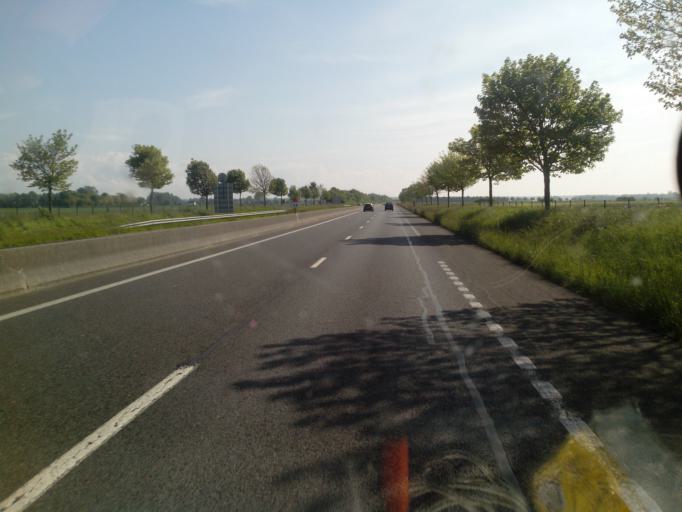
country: FR
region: Picardie
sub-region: Departement de la Somme
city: Bouttencourt
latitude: 49.9817
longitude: 1.6799
